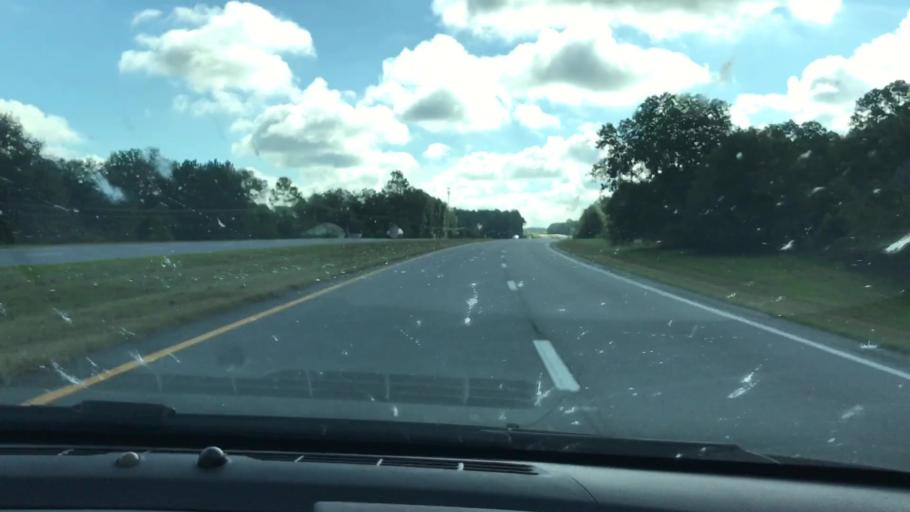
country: US
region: Georgia
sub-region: Worth County
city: Sylvester
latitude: 31.5528
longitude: -83.9502
